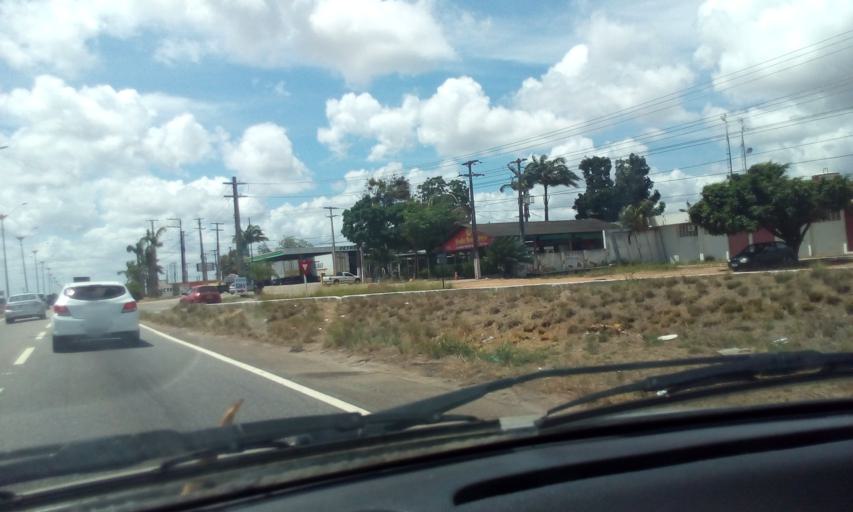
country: BR
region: Rio Grande do Norte
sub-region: Parnamirim
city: Parnamirim
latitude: -5.8937
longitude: -35.2576
